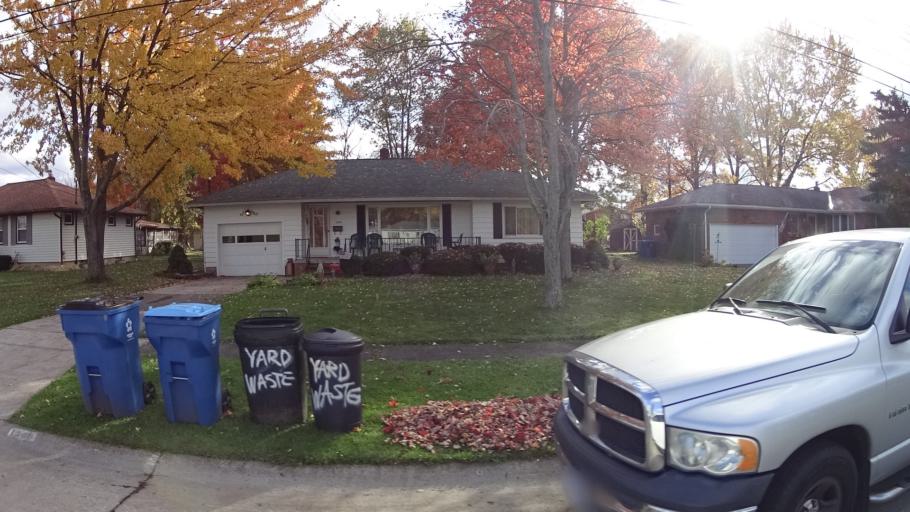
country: US
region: Ohio
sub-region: Lorain County
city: Lorain
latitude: 41.4237
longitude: -82.1882
